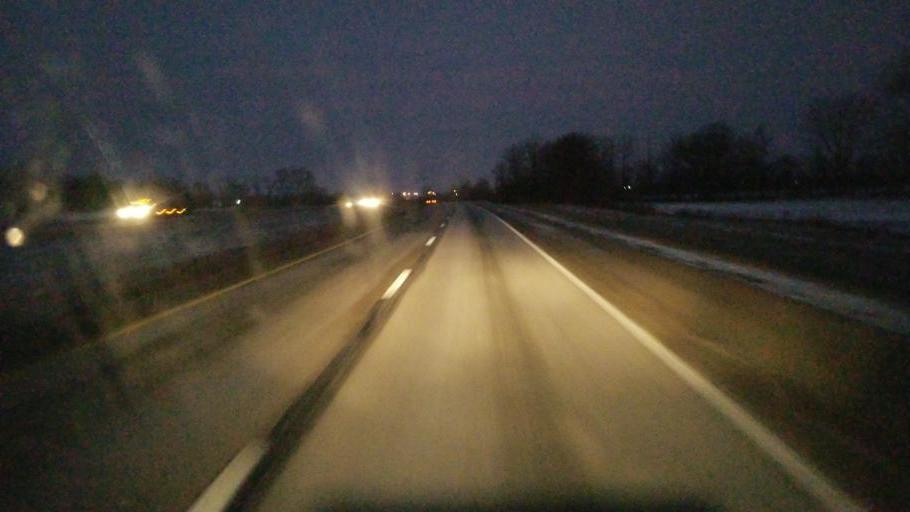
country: US
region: Ohio
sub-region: Preble County
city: New Paris
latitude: 39.8356
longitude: -84.7104
